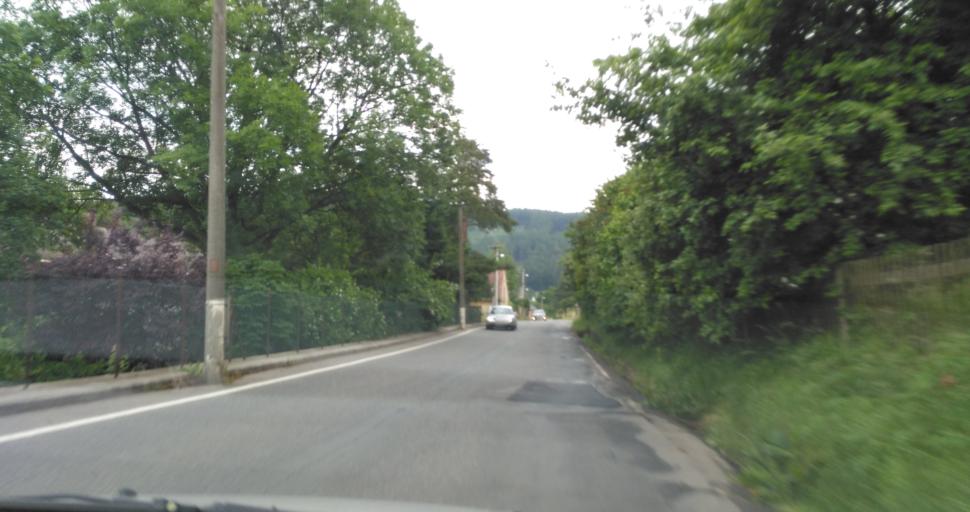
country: CZ
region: Central Bohemia
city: Jince
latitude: 49.7772
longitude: 13.9981
